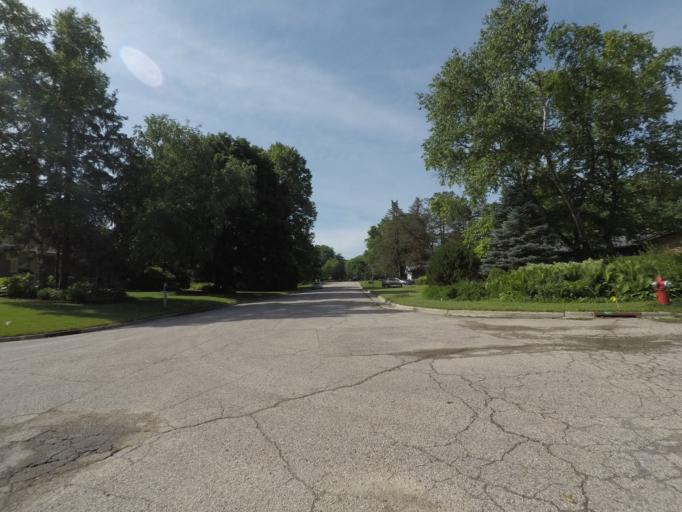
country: US
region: Wisconsin
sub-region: Dane County
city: Middleton
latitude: 43.0763
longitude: -89.4913
